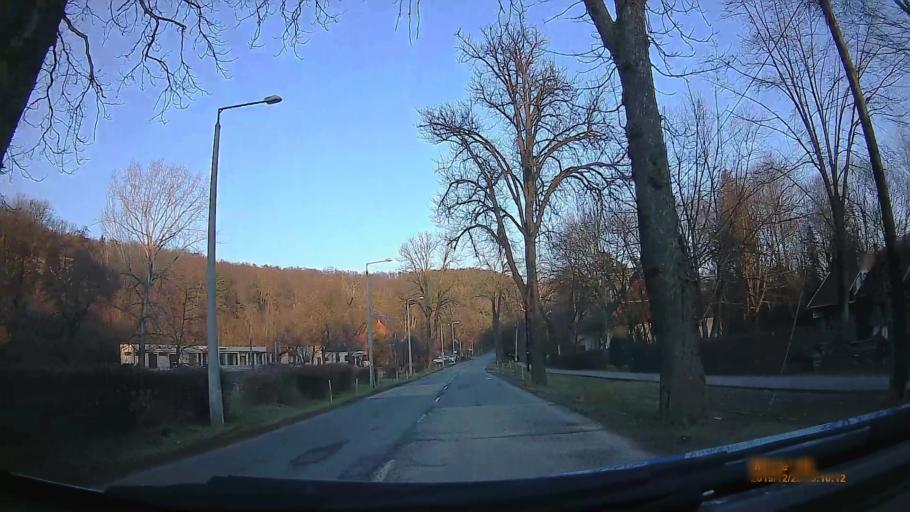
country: HU
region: Heves
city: Parad
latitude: 47.9241
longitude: 20.0542
